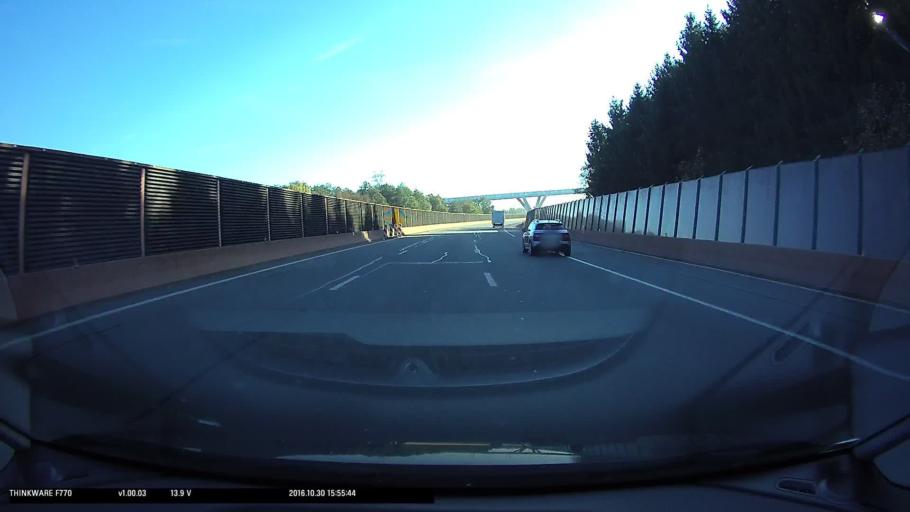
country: FR
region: Franche-Comte
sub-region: Territoire de Belfort
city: Chatenois-les-Forges
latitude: 47.5791
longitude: 6.8571
